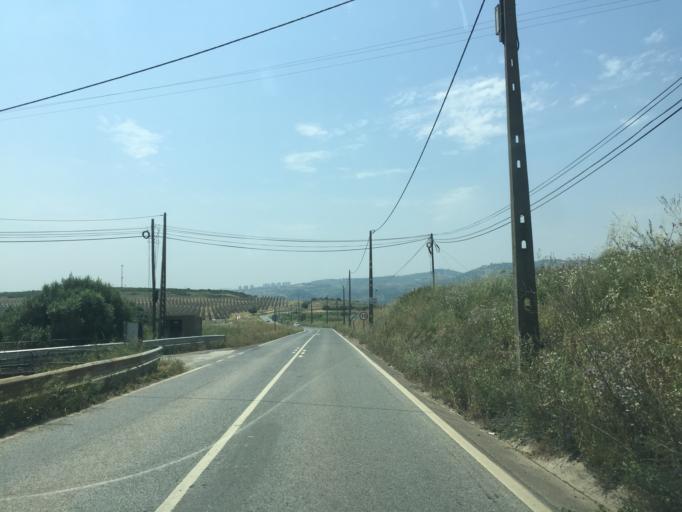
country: PT
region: Lisbon
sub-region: Loures
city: Loures
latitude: 38.8637
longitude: -9.1817
